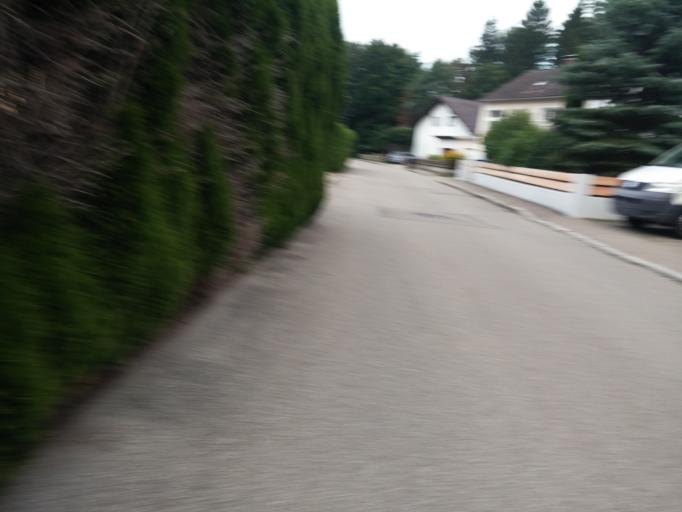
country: DE
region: Bavaria
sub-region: Swabia
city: Buxheim
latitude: 47.9954
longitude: 10.1260
